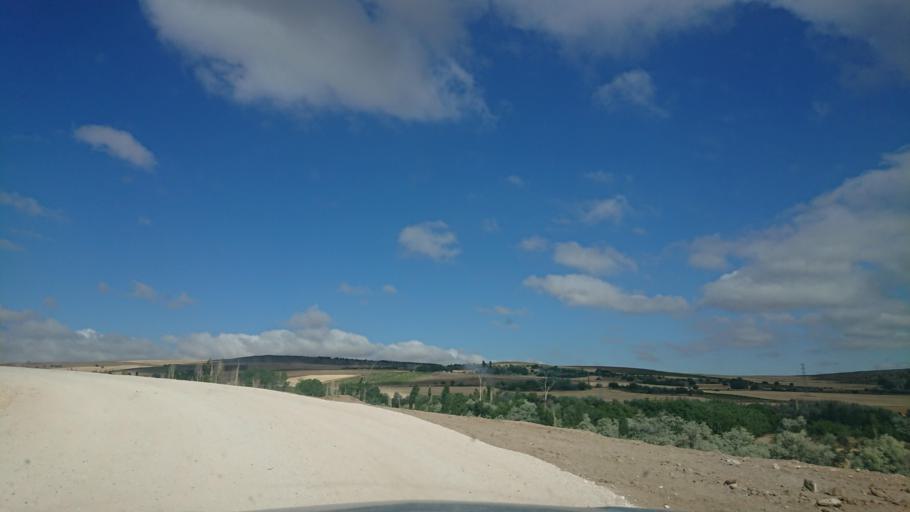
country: TR
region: Aksaray
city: Agacoren
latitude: 38.8584
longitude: 33.9429
